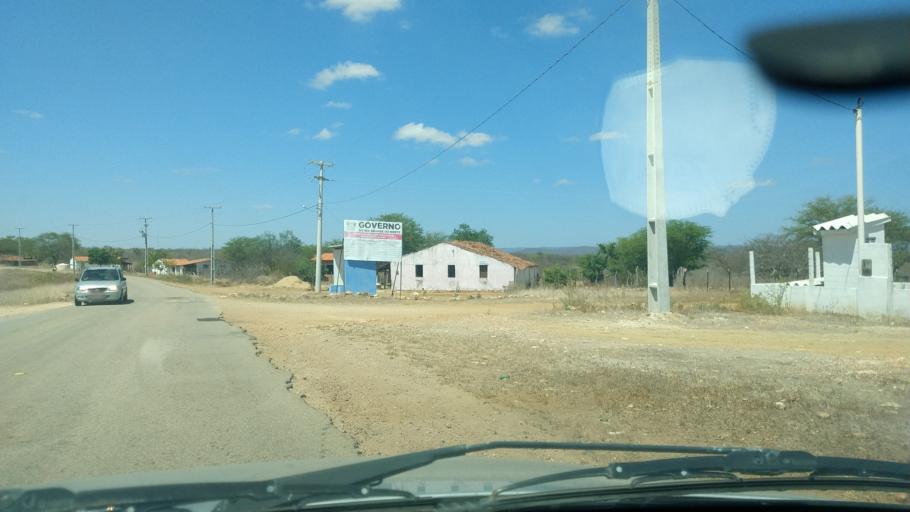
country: BR
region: Rio Grande do Norte
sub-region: Sao Tome
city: Sao Tome
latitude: -5.9670
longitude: -35.9691
